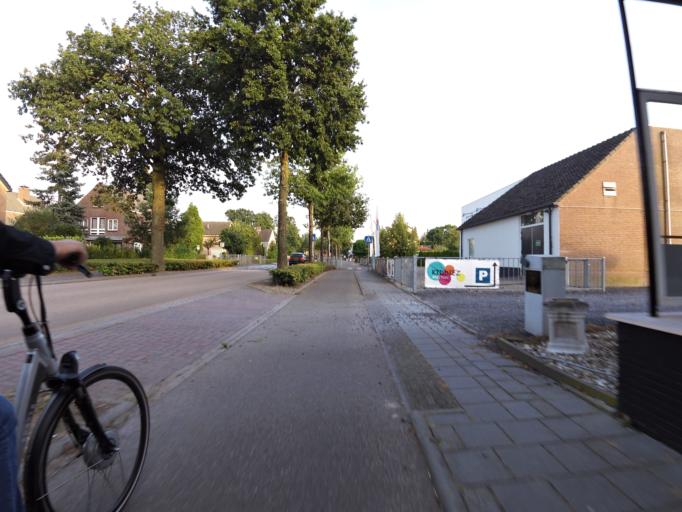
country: NL
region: Gelderland
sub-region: Gemeente Zevenaar
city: Zevenaar
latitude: 51.9071
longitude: 6.1116
